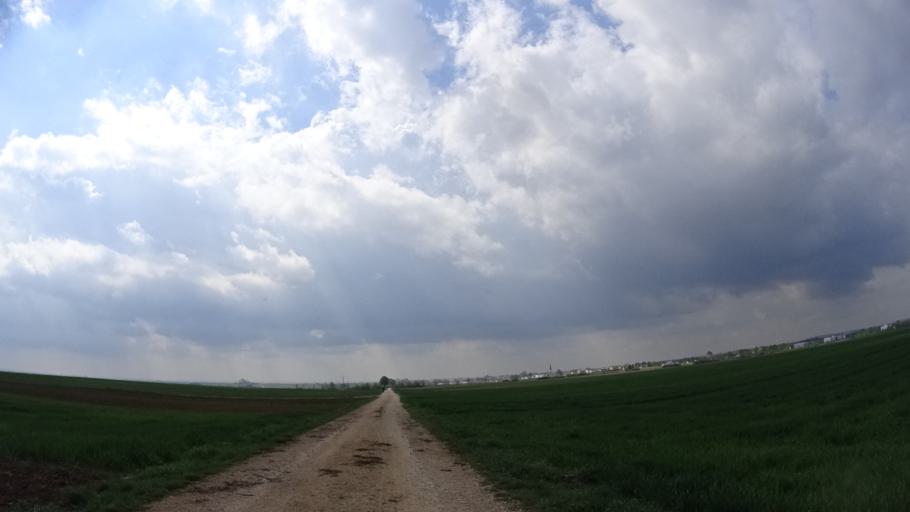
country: DE
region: Bavaria
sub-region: Upper Bavaria
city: Hitzhofen
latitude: 48.8340
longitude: 11.3299
